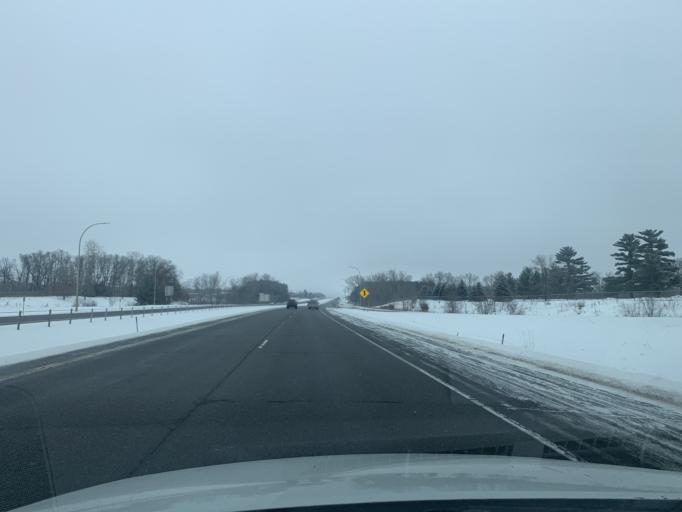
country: US
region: Minnesota
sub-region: Chisago County
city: North Branch
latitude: 45.5114
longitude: -92.9930
